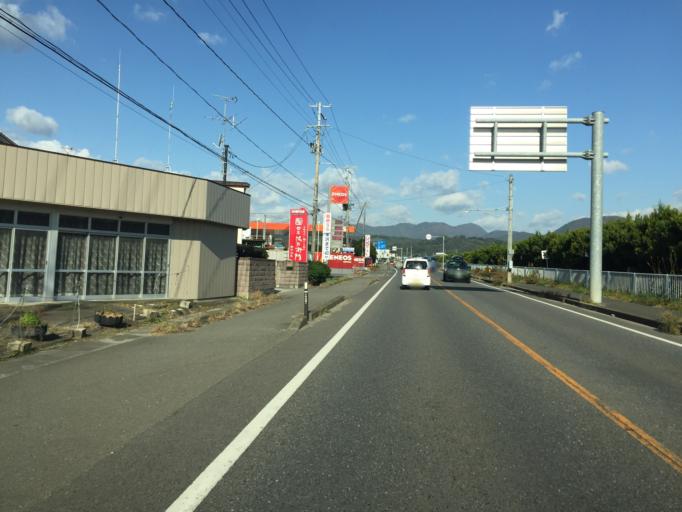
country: JP
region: Fukushima
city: Fukushima-shi
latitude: 37.8129
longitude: 140.4425
